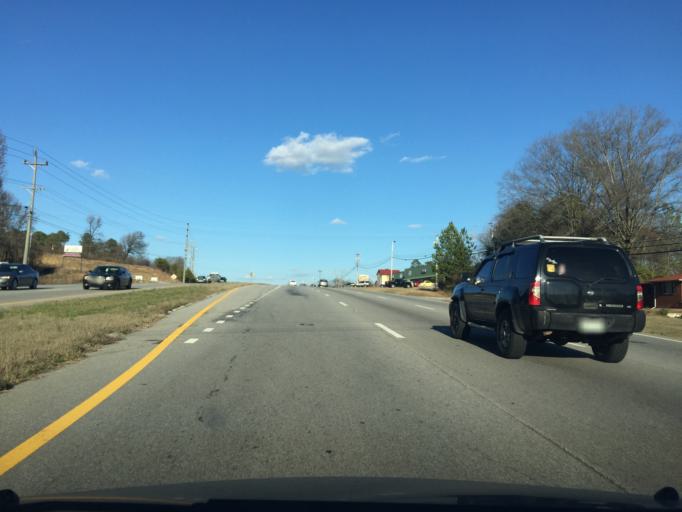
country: US
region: Tennessee
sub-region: Hamilton County
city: Harrison
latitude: 35.0950
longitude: -85.1766
